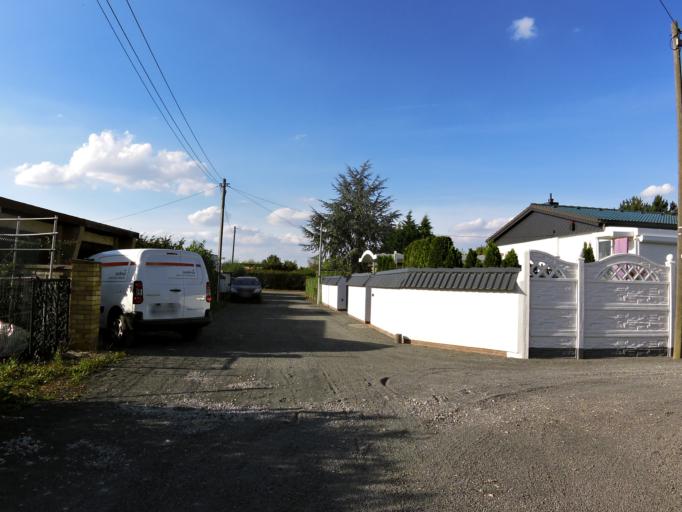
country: DE
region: Saxony
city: Schkeuditz
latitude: 51.3485
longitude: 12.2724
